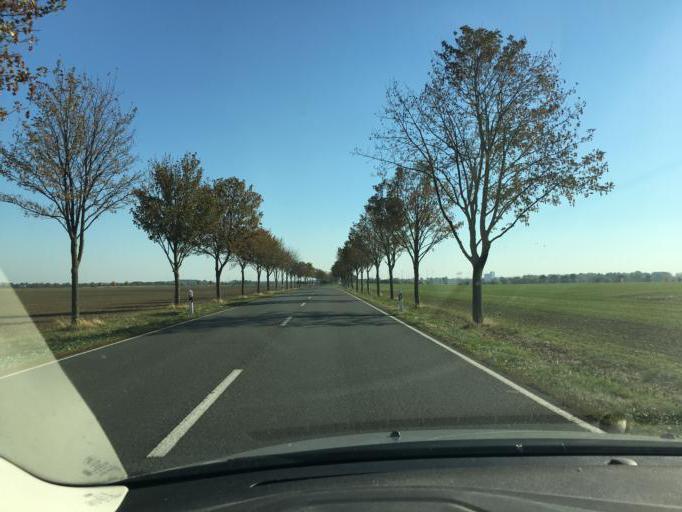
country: DE
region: Saxony-Anhalt
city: Wanzleben
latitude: 52.0207
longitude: 11.4974
